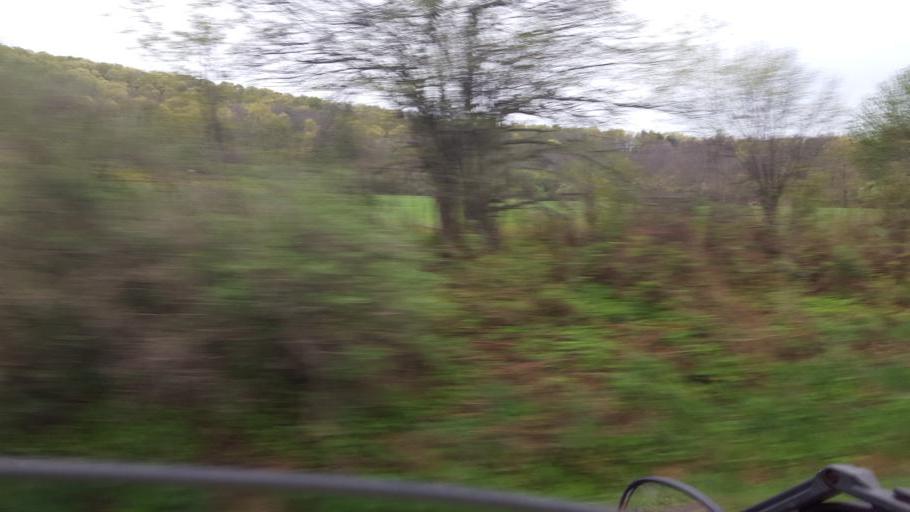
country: US
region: New York
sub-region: Allegany County
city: Andover
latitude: 41.9298
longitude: -77.7989
